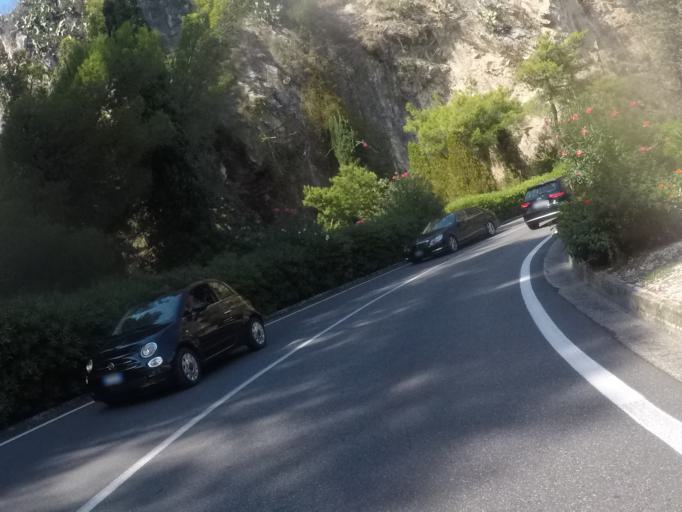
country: IT
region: Sicily
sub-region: Messina
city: Taormina
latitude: 37.8578
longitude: 15.2897
